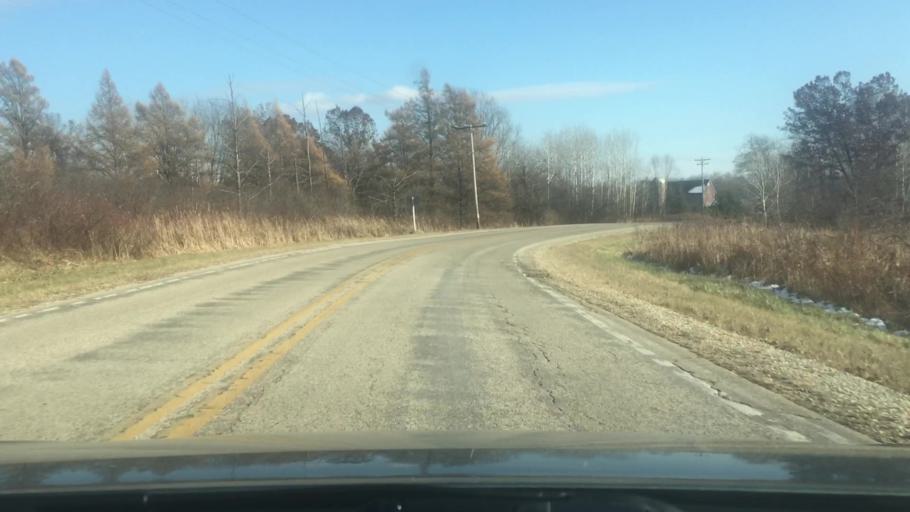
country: US
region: Wisconsin
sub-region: Jefferson County
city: Palmyra
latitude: 42.9393
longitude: -88.5915
